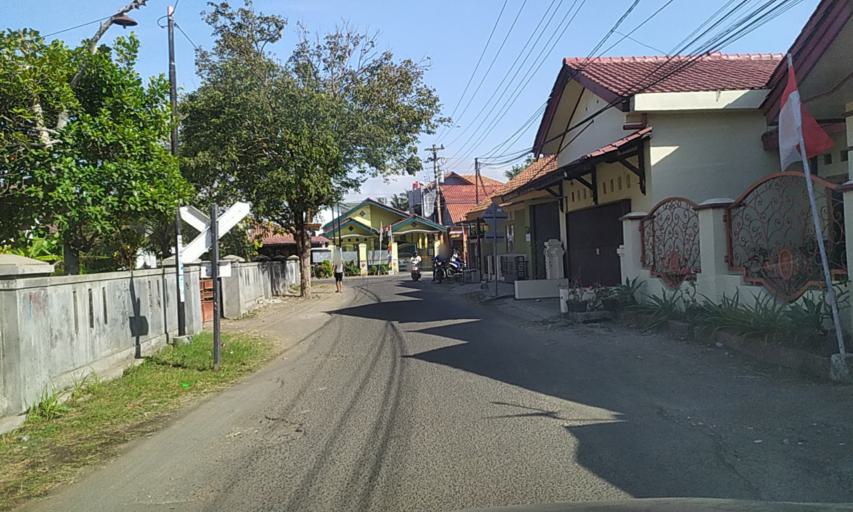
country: ID
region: Central Java
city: Karangbadar Kidul
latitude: -7.7097
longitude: 109.0177
